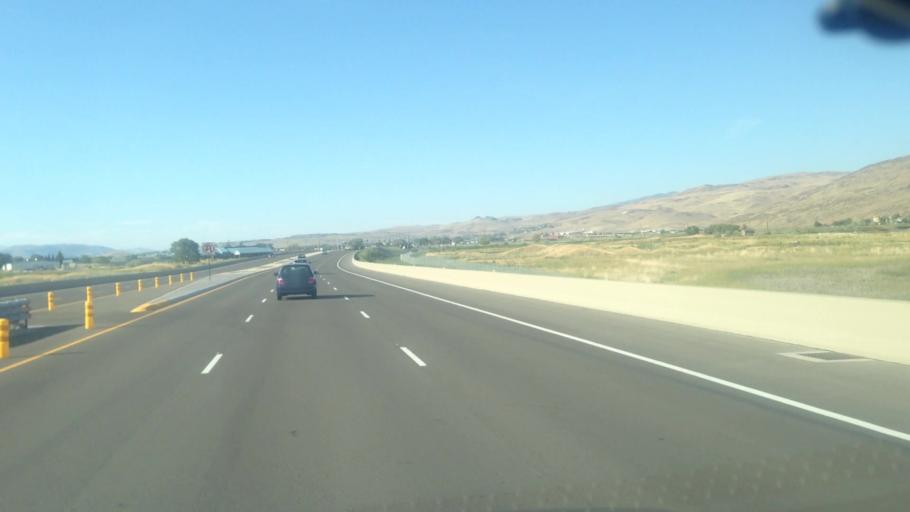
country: US
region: Nevada
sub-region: Washoe County
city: Sparks
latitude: 39.4928
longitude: -119.7320
